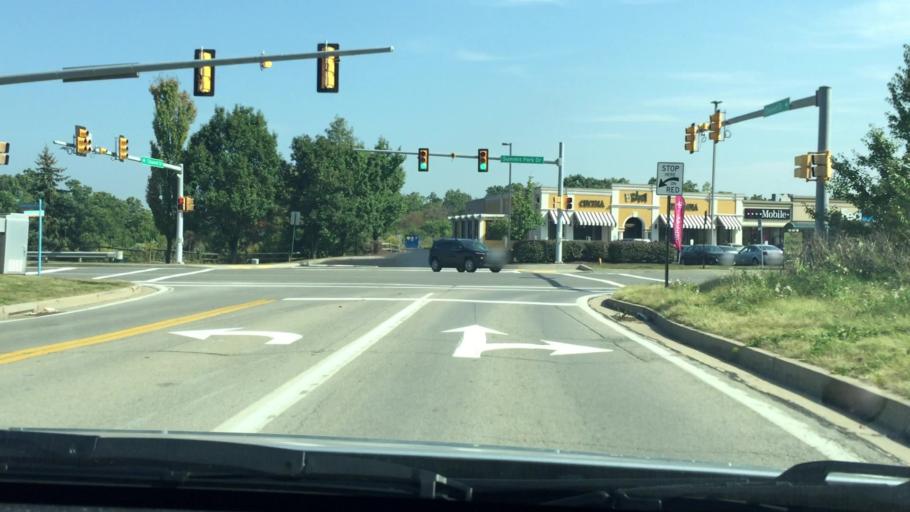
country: US
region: Pennsylvania
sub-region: Allegheny County
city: Oakdale
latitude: 40.4478
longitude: -80.1816
